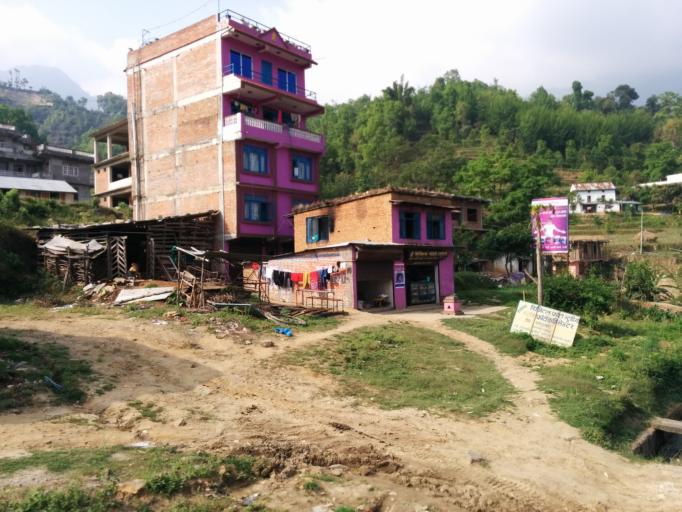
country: NP
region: Central Region
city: Kirtipur
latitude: 27.7174
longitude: 85.1589
